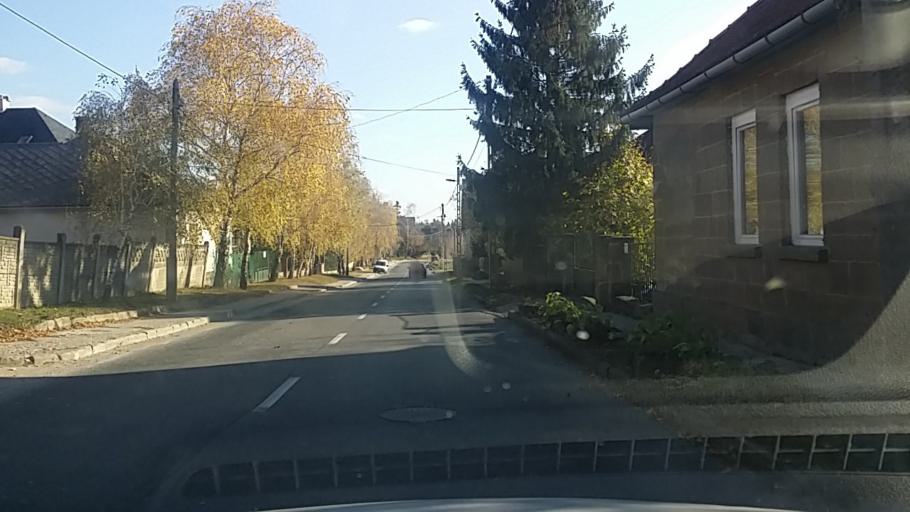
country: HU
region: Pest
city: Pilisszanto
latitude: 47.6657
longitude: 18.8909
